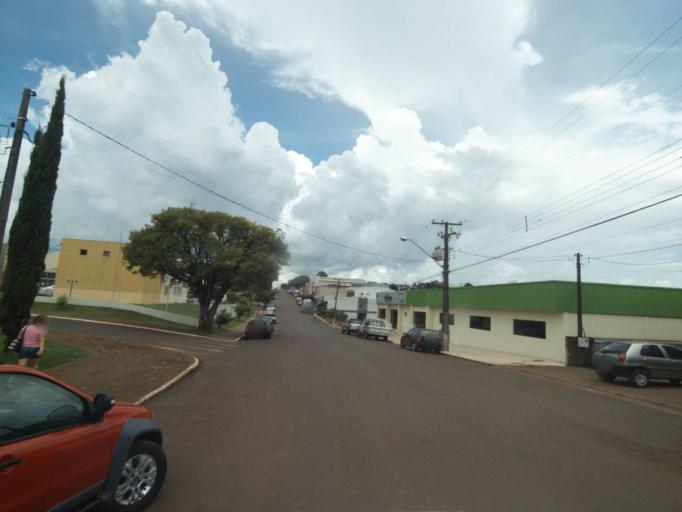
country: BR
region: Parana
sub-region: Guaraniacu
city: Guaraniacu
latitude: -25.1001
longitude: -52.8711
